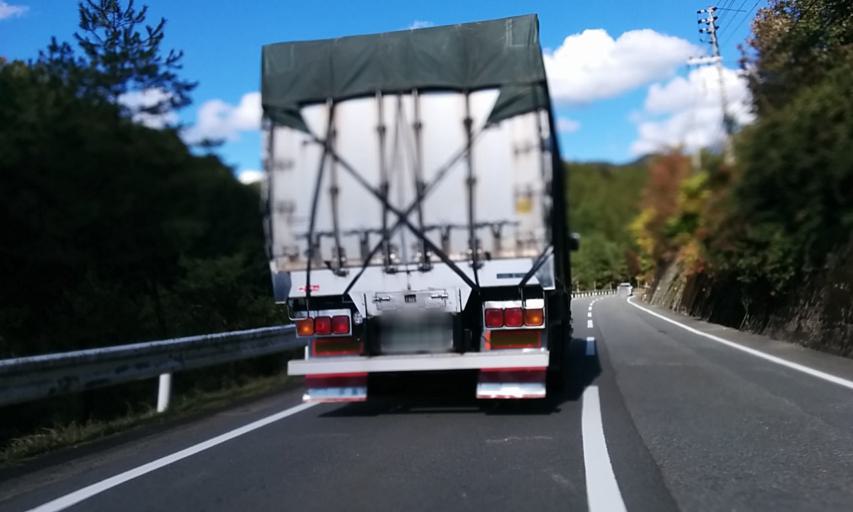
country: JP
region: Kyoto
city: Kameoka
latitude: 35.2020
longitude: 135.6168
